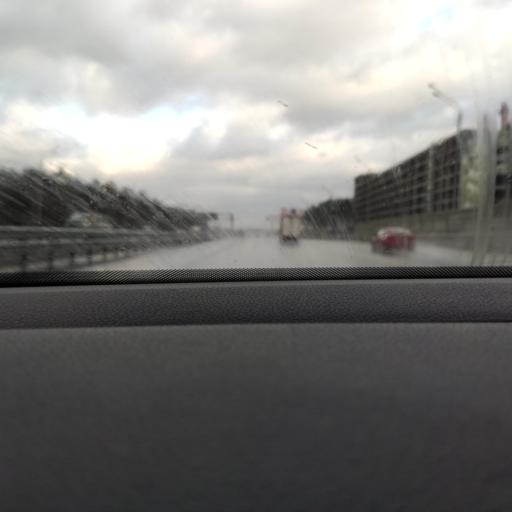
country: RU
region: Moskovskaya
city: Petrovo-Dal'neye
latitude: 55.7745
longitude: 37.2122
